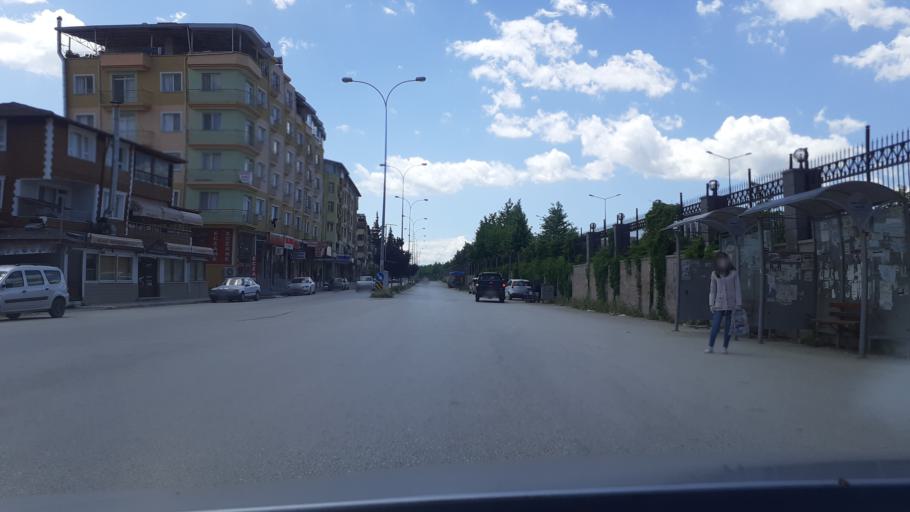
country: TR
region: Hatay
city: Anayazi
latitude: 36.3387
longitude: 36.2005
